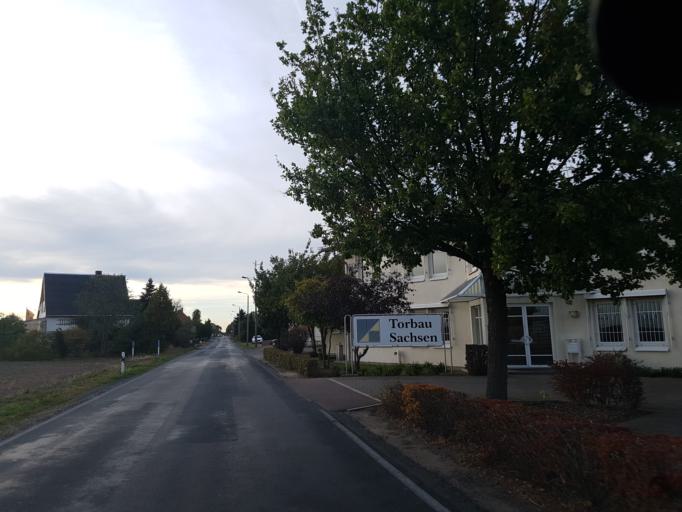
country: DE
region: Saxony
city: Wulknitz
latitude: 51.3679
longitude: 13.3959
